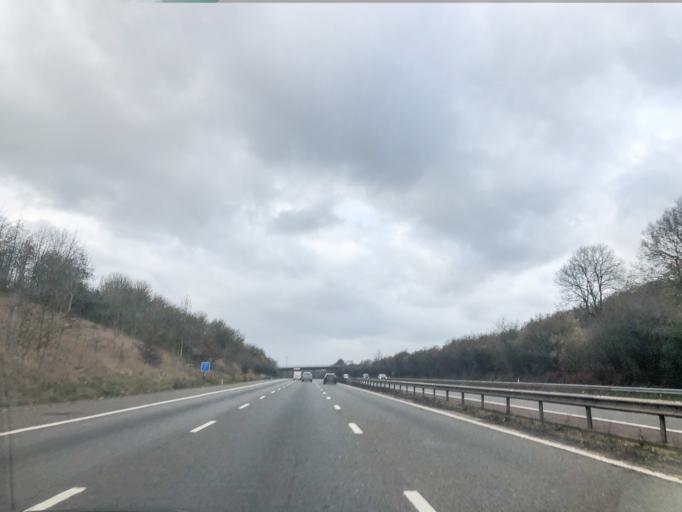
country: GB
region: England
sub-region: Warwickshire
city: Wroxall
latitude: 52.3142
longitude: -1.7141
